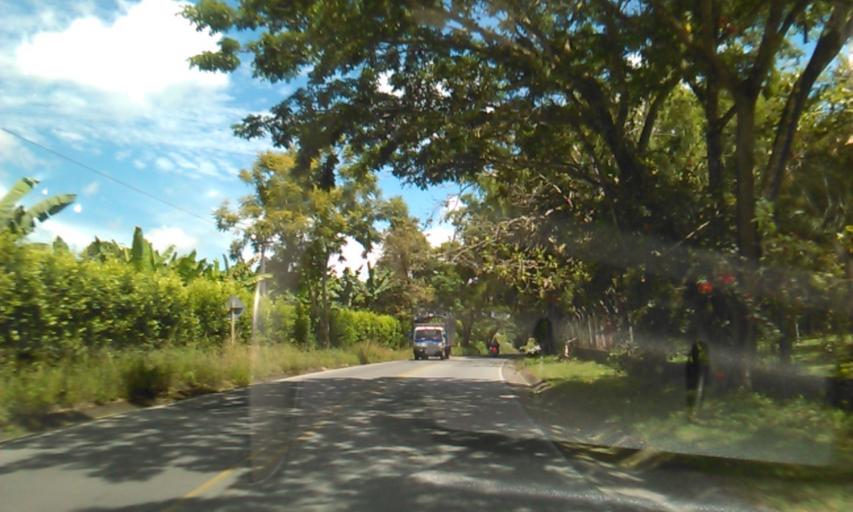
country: CO
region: Quindio
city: Cordoba
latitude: 4.4123
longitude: -75.7270
